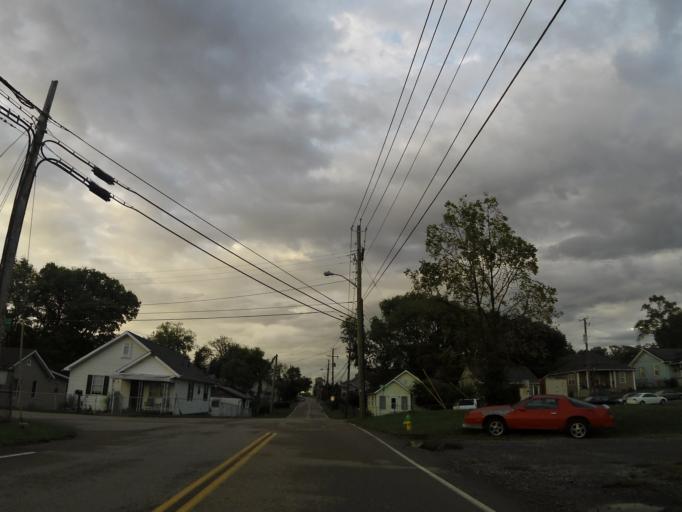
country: US
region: Tennessee
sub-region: Knox County
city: Knoxville
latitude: 35.9885
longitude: -83.9103
